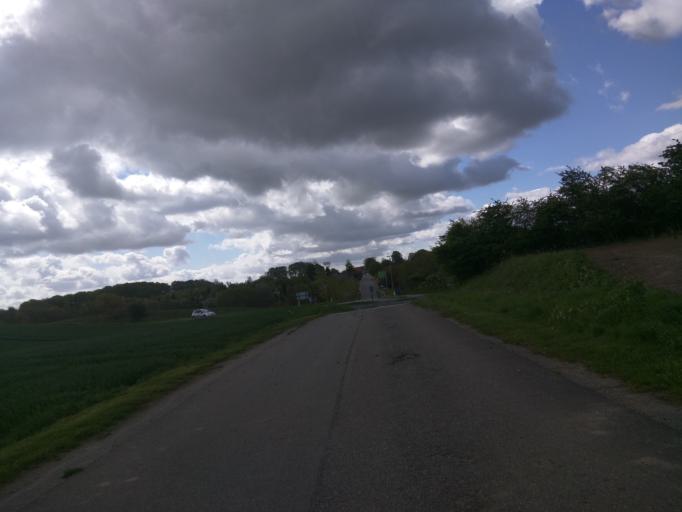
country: DK
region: Central Jutland
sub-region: Silkeborg Kommune
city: Kjellerup
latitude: 56.2975
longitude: 9.4266
